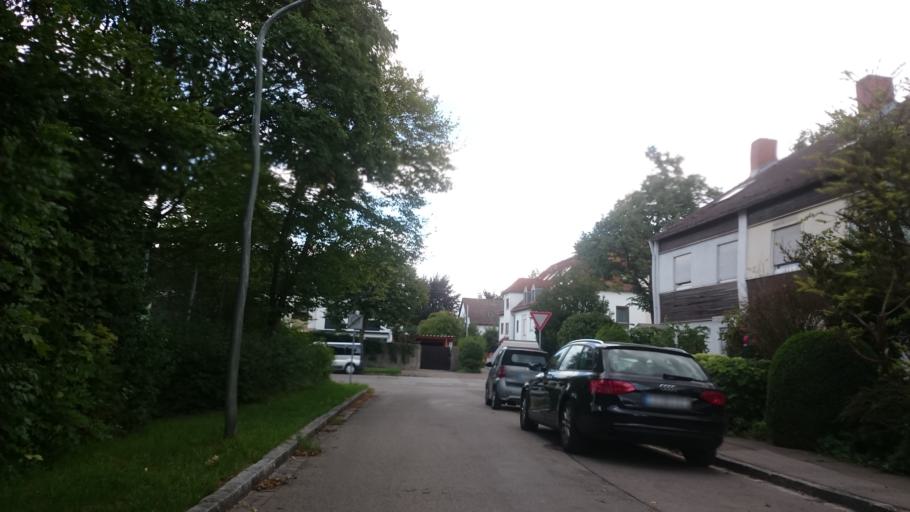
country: DE
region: Bavaria
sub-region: Swabia
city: Augsburg
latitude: 48.3591
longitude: 10.9406
